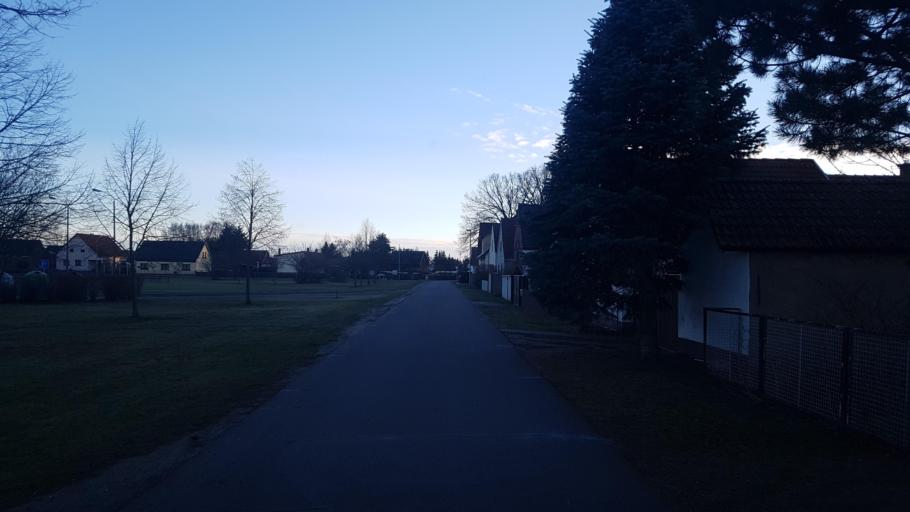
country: DE
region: Brandenburg
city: Drachhausen
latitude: 51.8922
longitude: 14.3117
